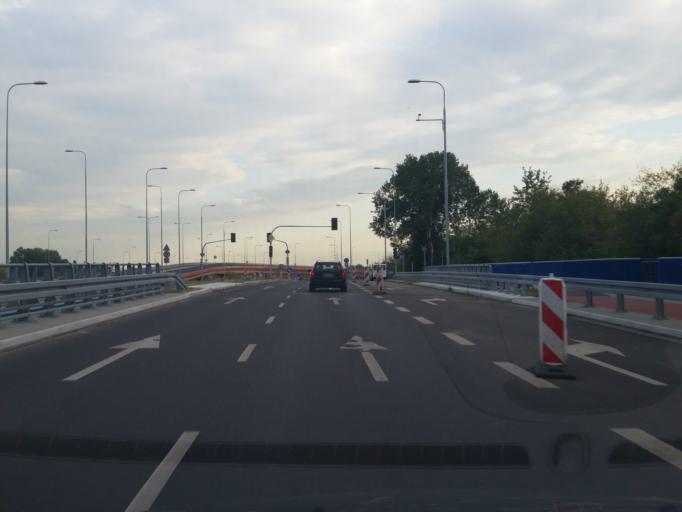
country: PL
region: Masovian Voivodeship
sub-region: Warszawa
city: Wlochy
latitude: 52.1714
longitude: 20.9853
